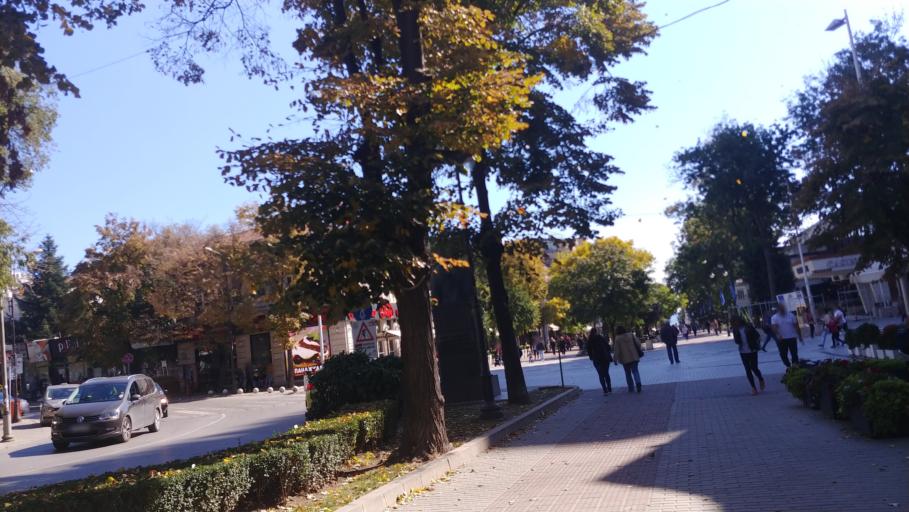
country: BG
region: Varna
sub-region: Obshtina Varna
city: Varna
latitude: 43.2060
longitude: 27.9191
